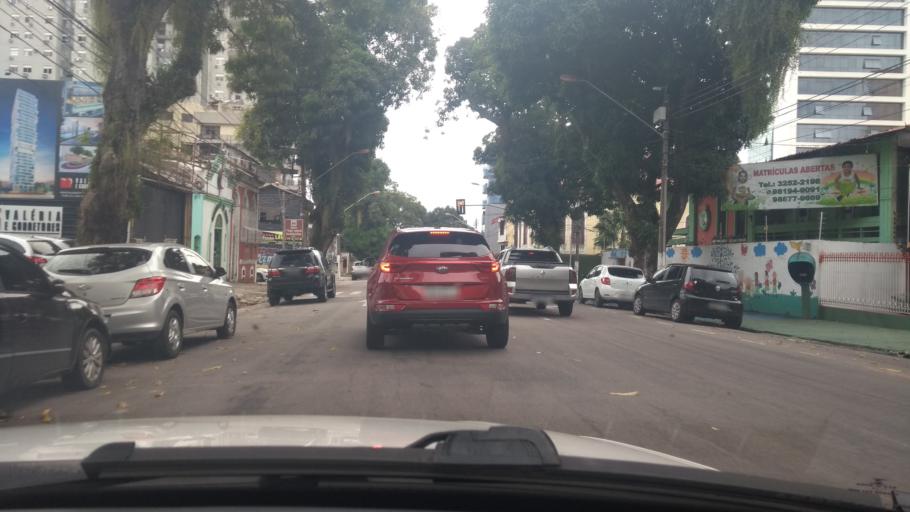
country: BR
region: Para
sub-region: Belem
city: Belem
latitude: -1.4613
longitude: -48.4935
